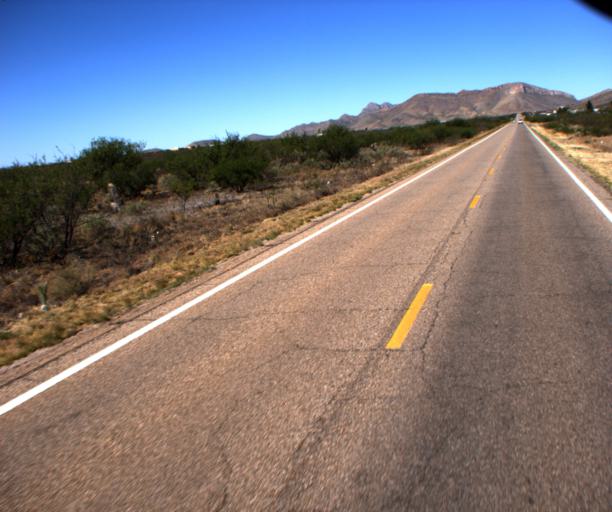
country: US
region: Arizona
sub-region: Cochise County
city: Huachuca City
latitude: 31.6924
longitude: -110.3689
